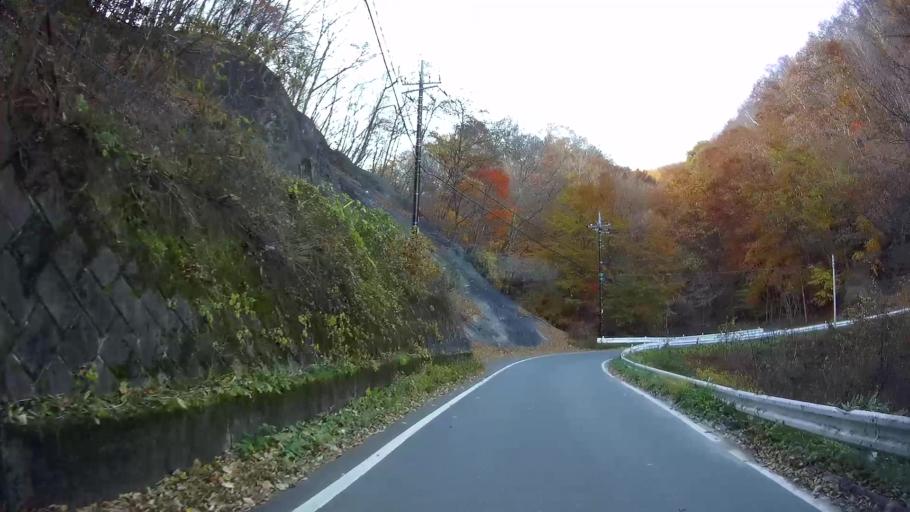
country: JP
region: Gunma
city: Nakanojomachi
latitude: 36.6687
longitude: 138.6693
